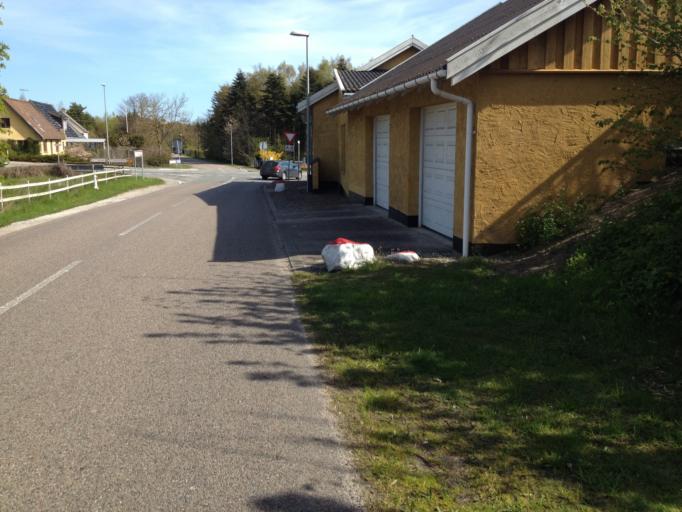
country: DK
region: Capital Region
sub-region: Halsnaes Kommune
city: Hundested
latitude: 55.9598
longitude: 11.9026
